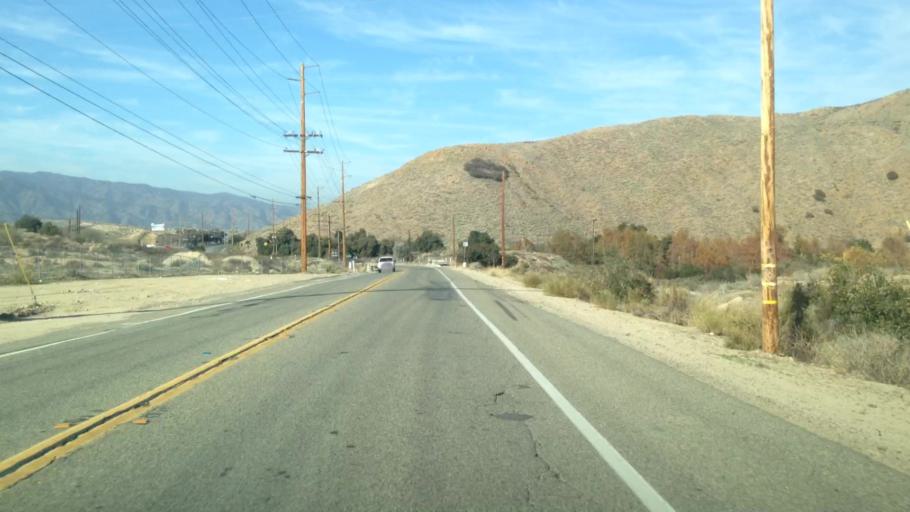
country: US
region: California
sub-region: Riverside County
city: El Cerrito
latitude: 33.7476
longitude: -117.4457
